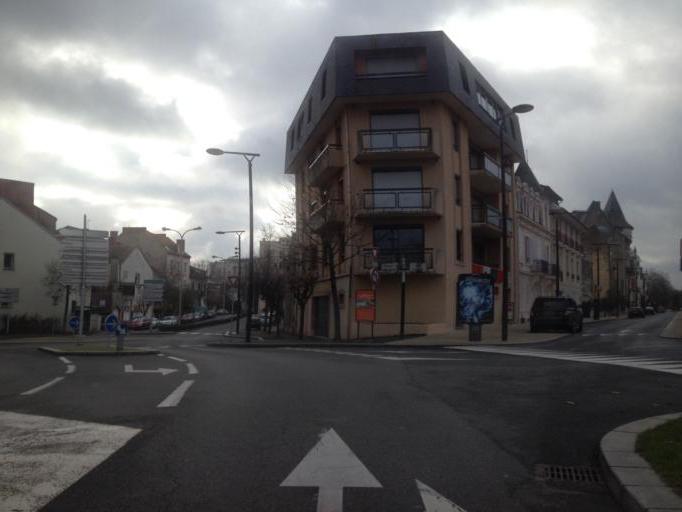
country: FR
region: Auvergne
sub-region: Departement de l'Allier
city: Vichy
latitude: 46.1290
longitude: 3.4163
